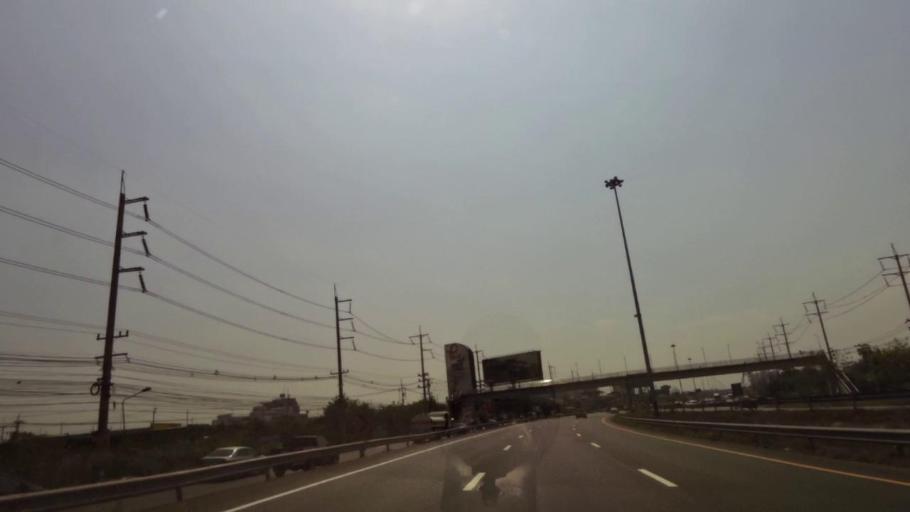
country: TH
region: Chon Buri
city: Chon Buri
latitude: 13.4273
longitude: 101.0031
